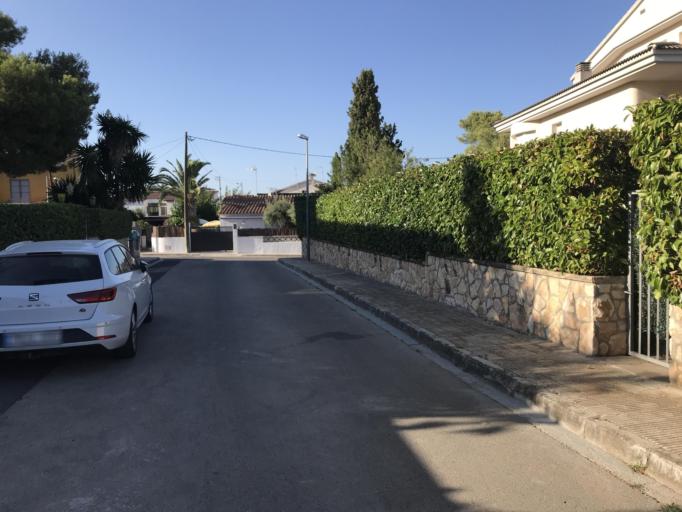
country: ES
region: Catalonia
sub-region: Provincia de Tarragona
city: Torredembarra
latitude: 41.1370
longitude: 1.3977
